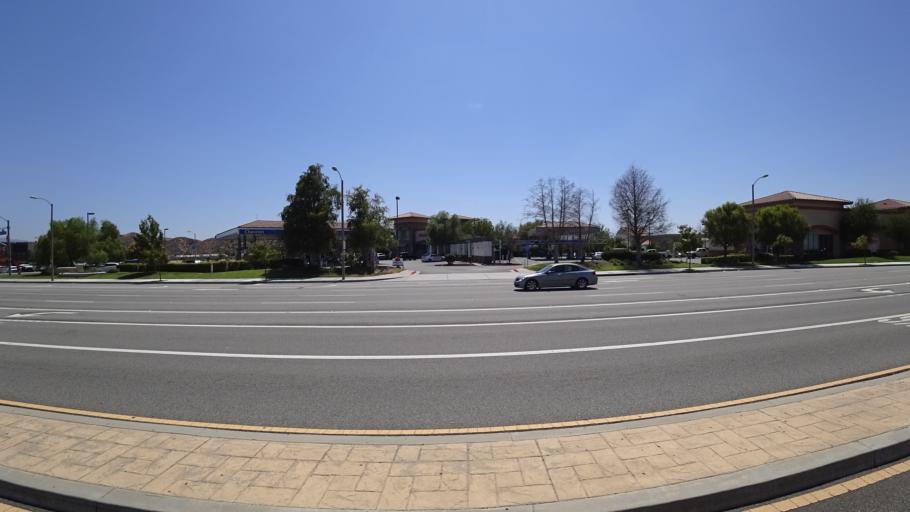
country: US
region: California
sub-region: Los Angeles County
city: Santa Clarita
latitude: 34.4277
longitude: -118.5380
